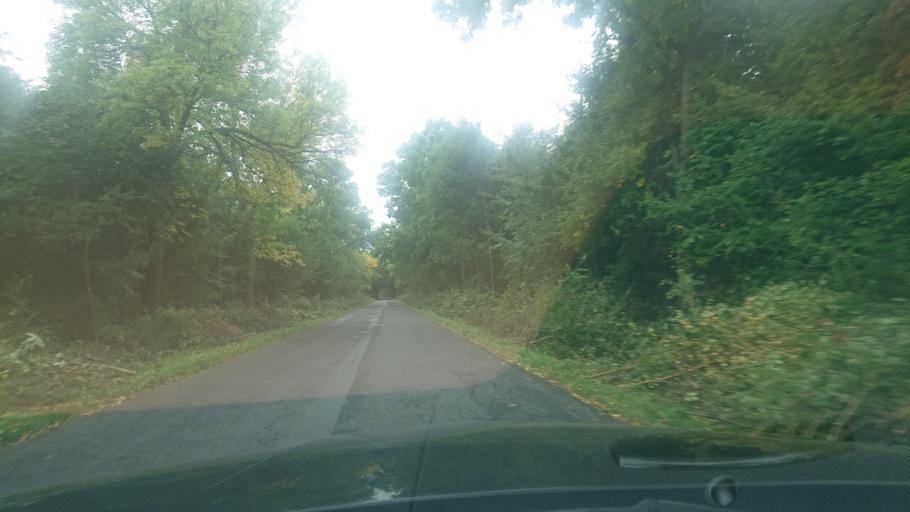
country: PL
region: Lower Silesian Voivodeship
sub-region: Powiat klodzki
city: Miedzylesie
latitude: 50.2225
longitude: 16.7186
